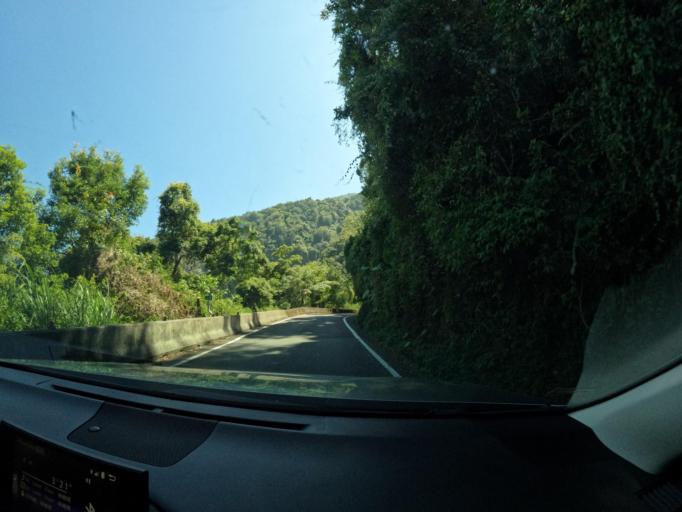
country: TW
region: Taiwan
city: Yujing
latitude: 23.2817
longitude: 120.8650
